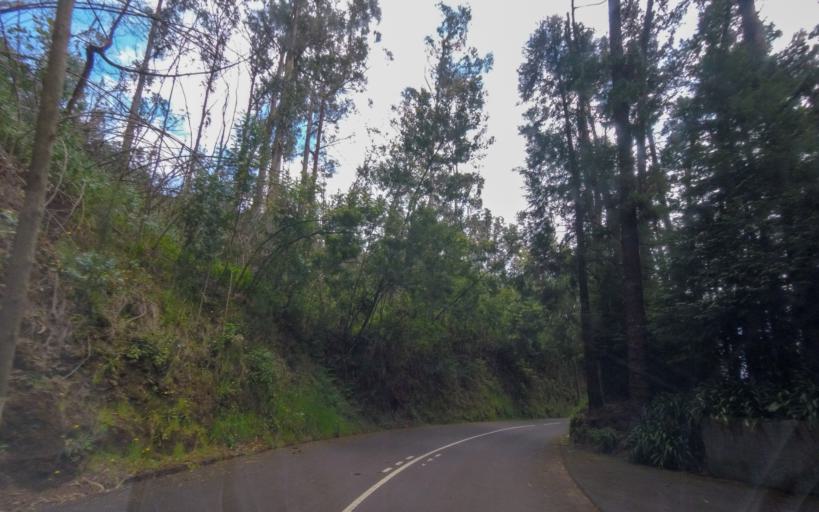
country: PT
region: Madeira
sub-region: Funchal
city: Nossa Senhora do Monte
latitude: 32.6739
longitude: -16.8826
